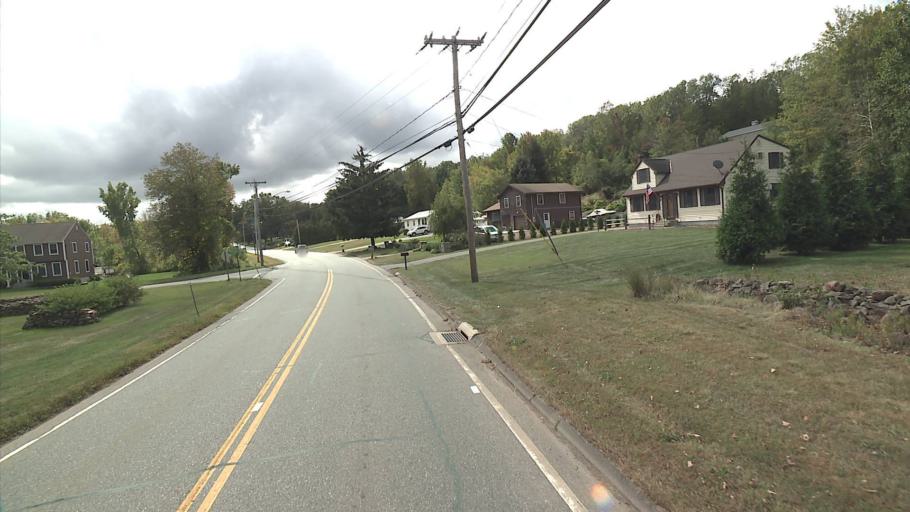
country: US
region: Connecticut
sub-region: Middlesex County
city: Durham
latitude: 41.5072
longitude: -72.7168
